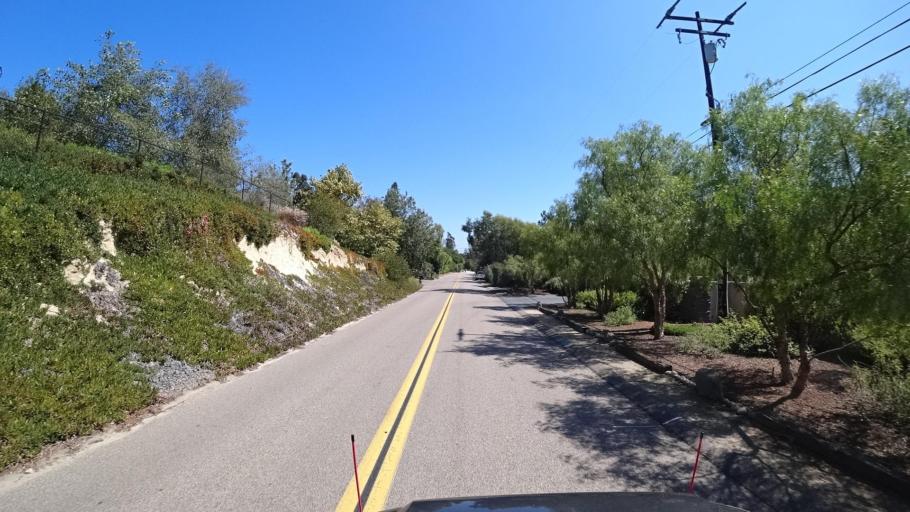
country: US
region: California
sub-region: San Diego County
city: Rancho Santa Fe
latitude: 32.9940
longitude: -117.2319
